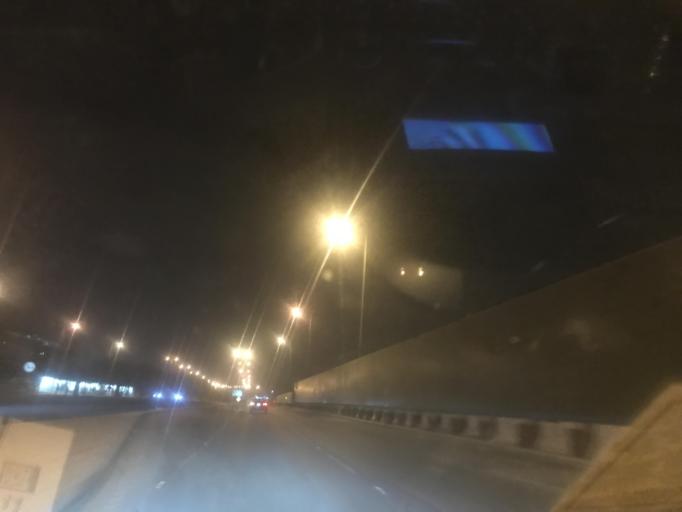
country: SA
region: Ar Riyad
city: Riyadh
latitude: 24.7908
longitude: 46.5884
